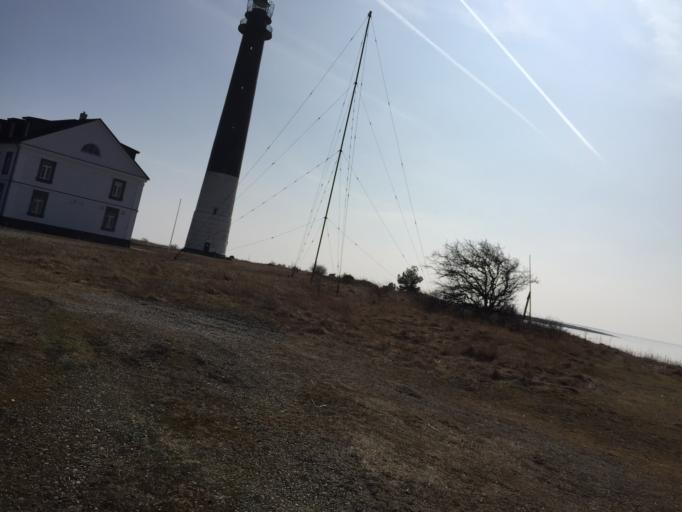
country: LV
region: Dundaga
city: Dundaga
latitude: 57.9109
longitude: 22.0548
